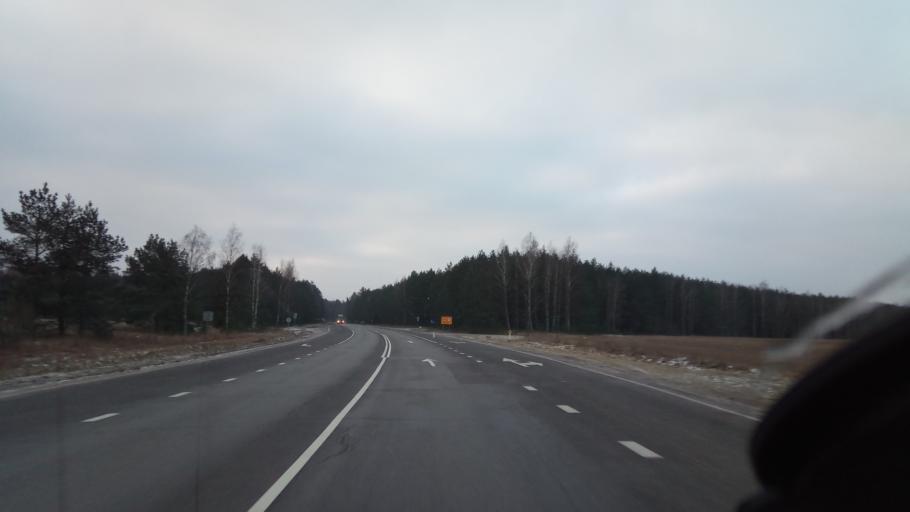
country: LT
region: Vilnius County
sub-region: Trakai
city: Rudiskes
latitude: 54.4275
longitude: 24.9792
